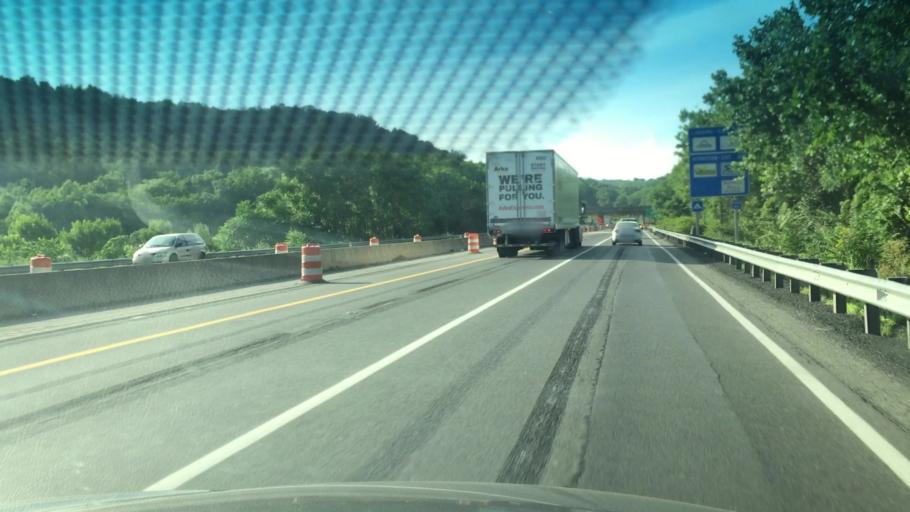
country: US
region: Pennsylvania
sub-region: Monroe County
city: East Stroudsburg
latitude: 40.9905
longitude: -75.1406
